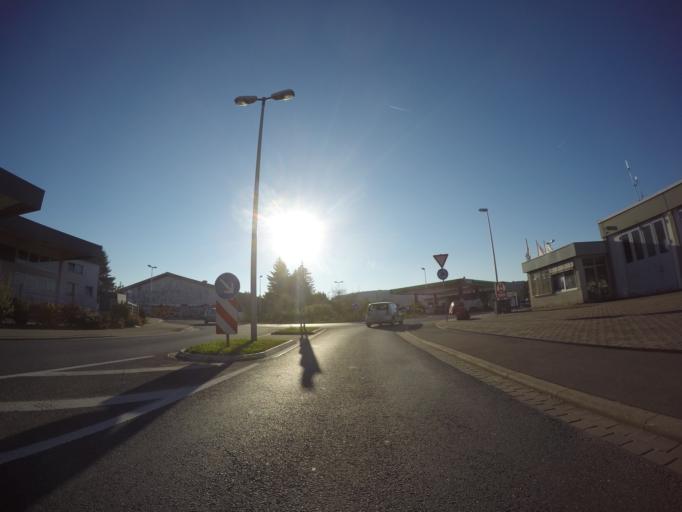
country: DE
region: Bavaria
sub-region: Regierungsbezirk Unterfranken
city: Marktheidenfeld
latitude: 49.8515
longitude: 9.6108
